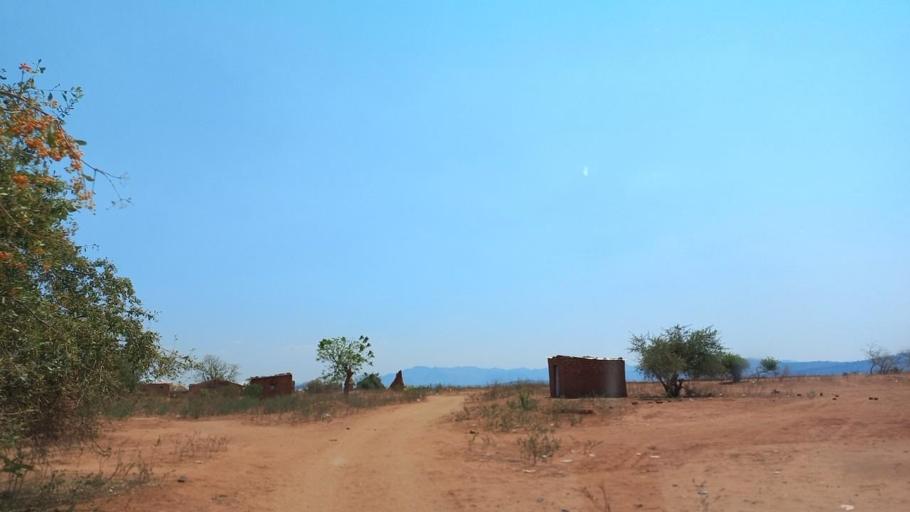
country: ZM
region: Lusaka
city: Luangwa
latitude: -15.6057
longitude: 30.4007
